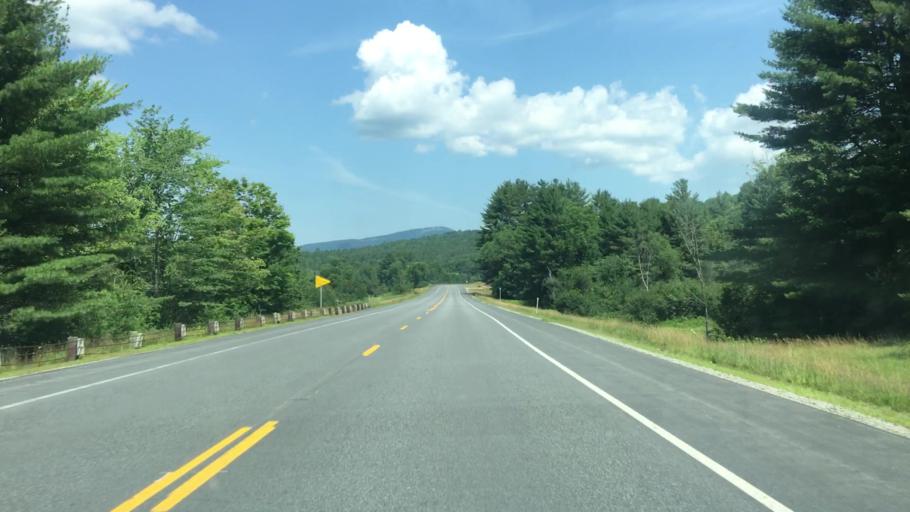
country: US
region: New Hampshire
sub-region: Sullivan County
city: Newport
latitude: 43.4069
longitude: -72.1858
